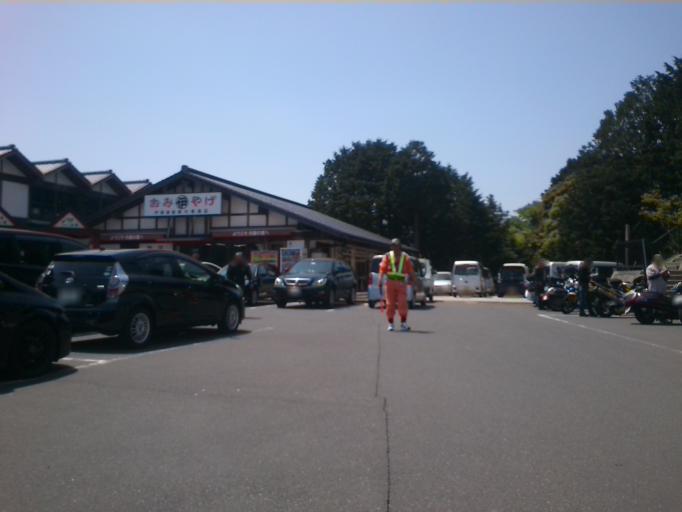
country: JP
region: Kyoto
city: Miyazu
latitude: 35.6748
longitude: 135.2915
